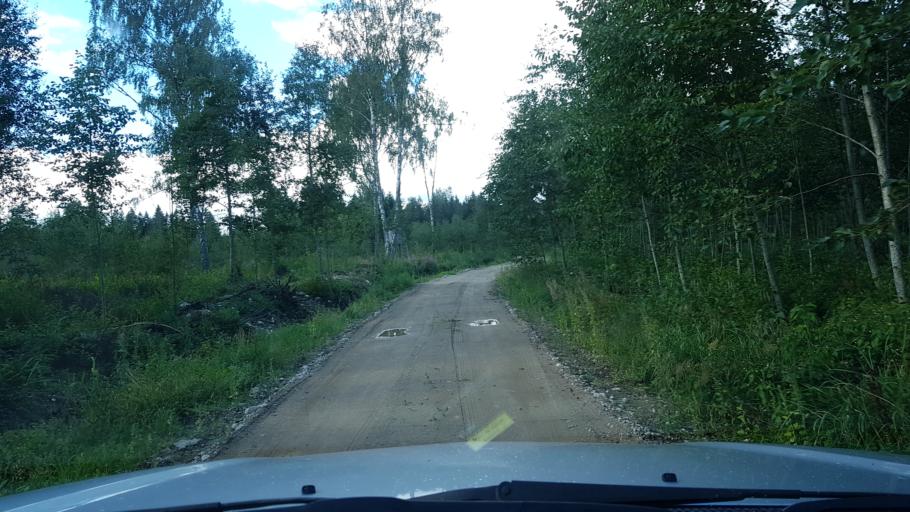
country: EE
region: Harju
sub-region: Raasiku vald
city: Arukula
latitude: 59.2548
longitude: 25.1001
